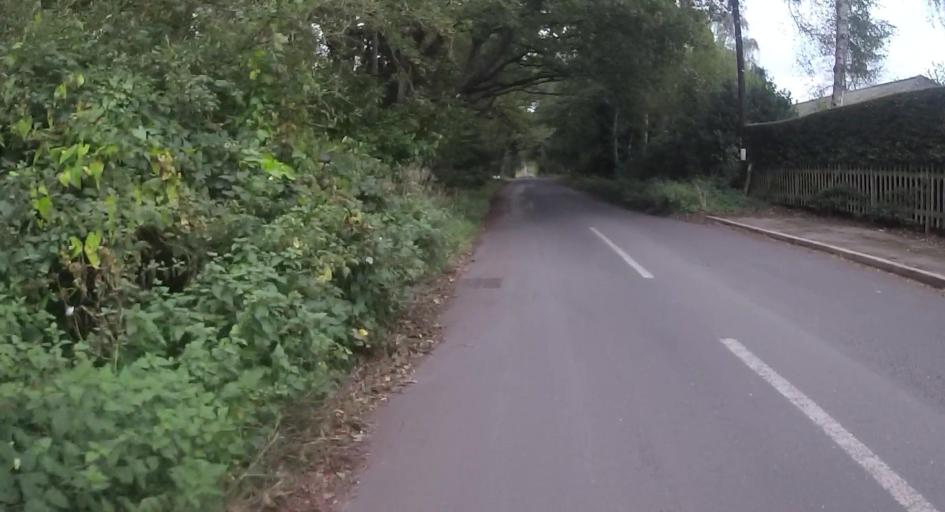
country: GB
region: England
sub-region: Hampshire
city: Fleet
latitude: 51.2810
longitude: -0.8815
